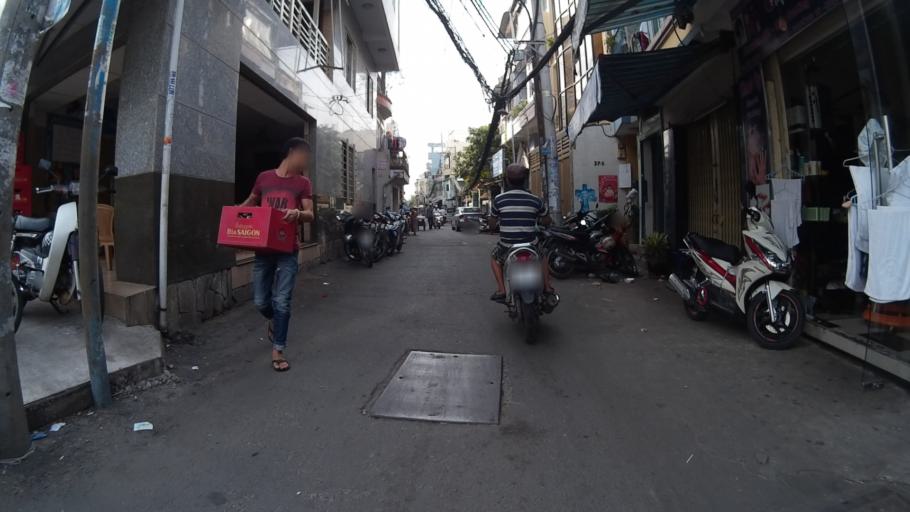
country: VN
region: Ho Chi Minh City
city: Quan Binh Thanh
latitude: 10.7947
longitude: 106.7012
